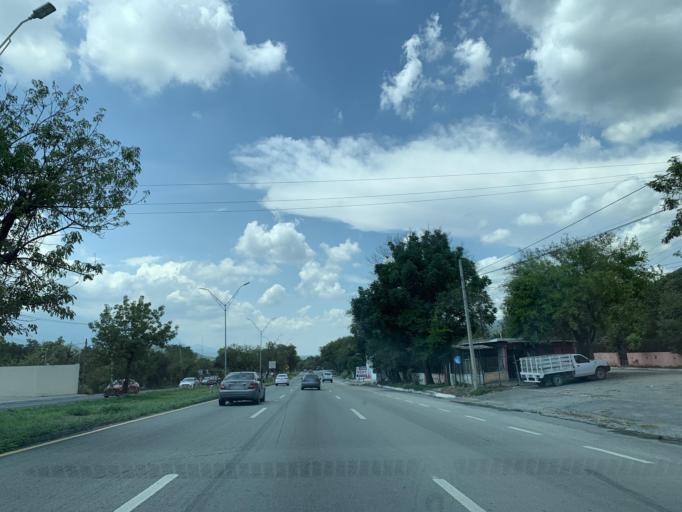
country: MX
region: Nuevo Leon
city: Santiago
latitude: 25.3929
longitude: -100.1205
